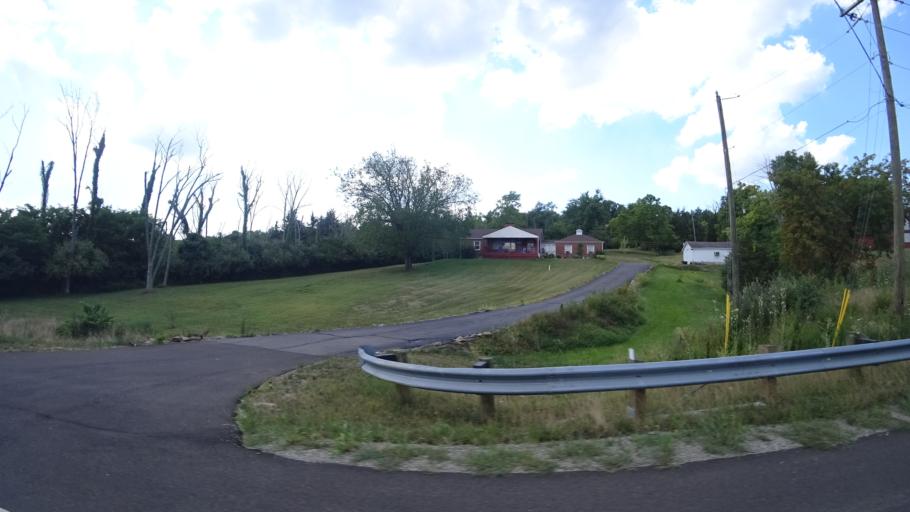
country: US
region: Ohio
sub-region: Butler County
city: Hamilton
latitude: 39.4378
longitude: -84.6076
